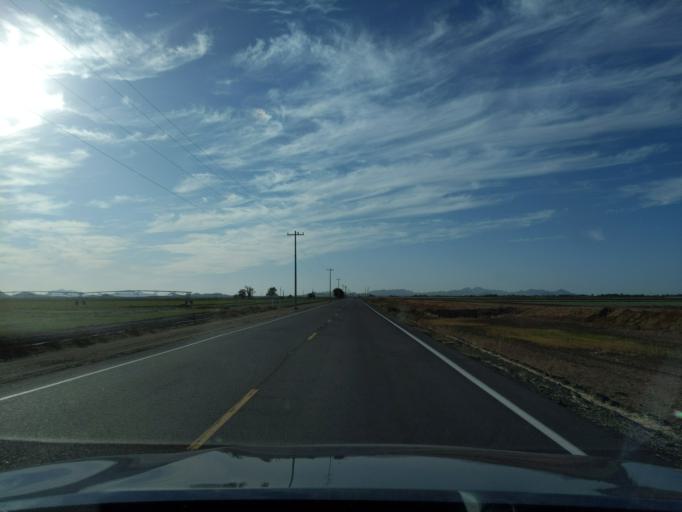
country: US
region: Arizona
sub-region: Pinal County
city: Florence
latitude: 33.1184
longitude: -111.4170
